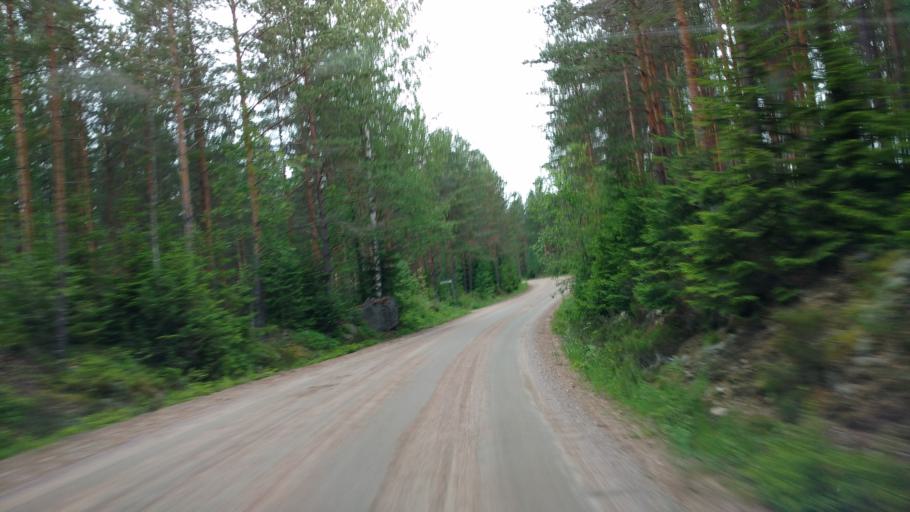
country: FI
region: Varsinais-Suomi
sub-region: Salo
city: Kiikala
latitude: 60.4849
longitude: 23.6608
